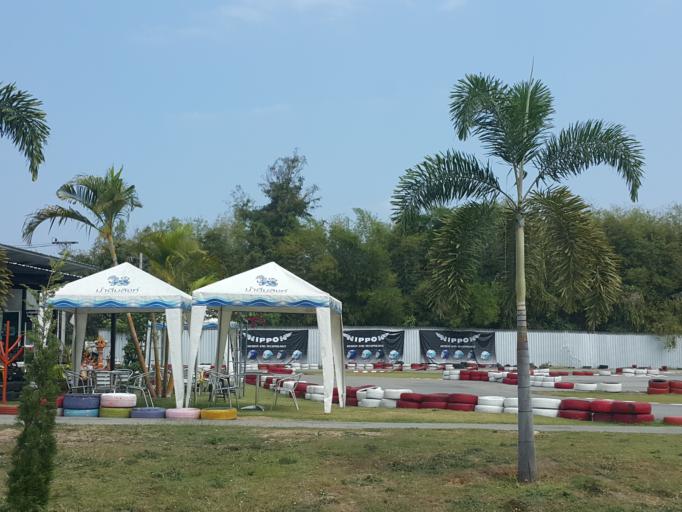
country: TH
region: Chiang Mai
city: Hang Dong
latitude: 18.7380
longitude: 98.9344
